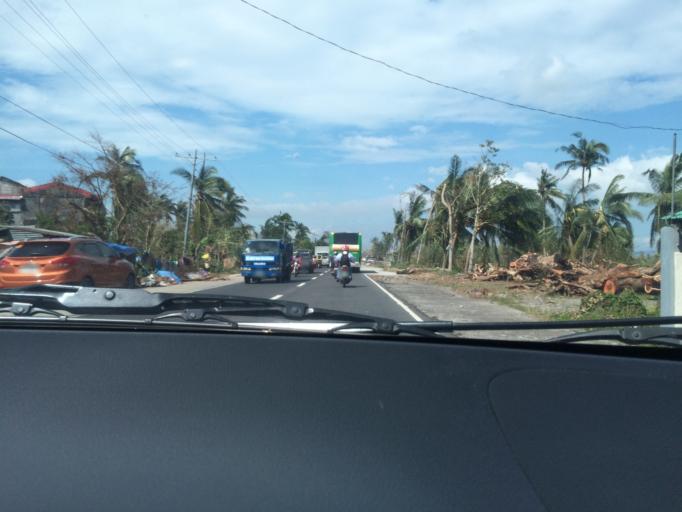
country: PH
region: Bicol
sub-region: Province of Albay
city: Iraya
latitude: 13.2600
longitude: 123.5000
